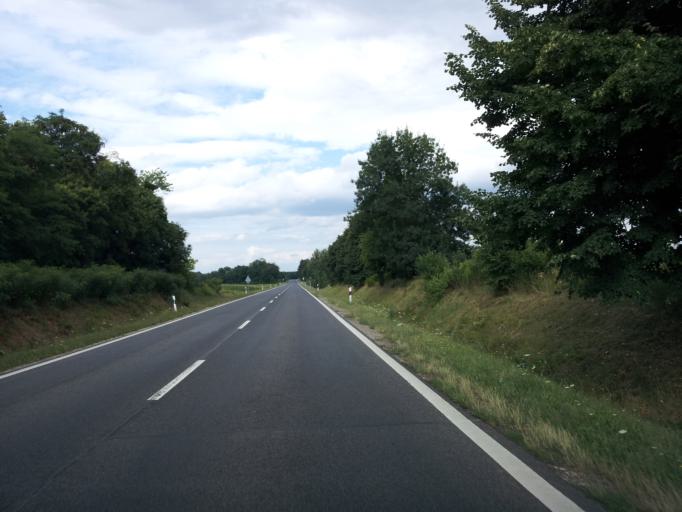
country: HU
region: Vas
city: Janoshaza
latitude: 47.1056
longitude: 17.0919
